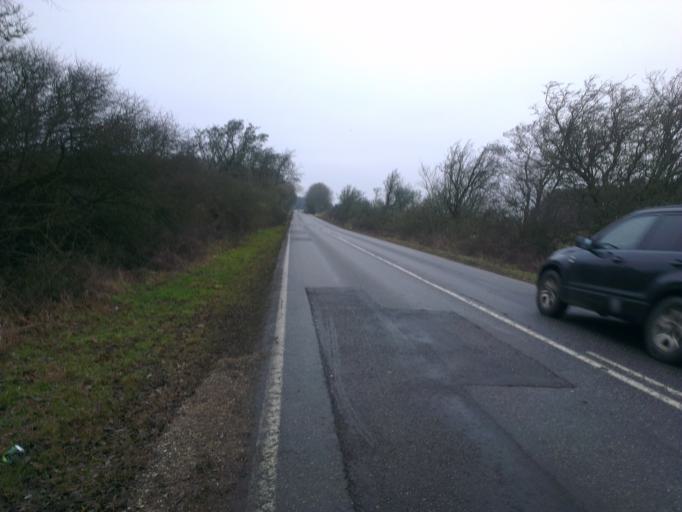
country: DK
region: Capital Region
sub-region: Frederikssund Kommune
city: Jaegerspris
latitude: 55.8700
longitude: 11.9625
